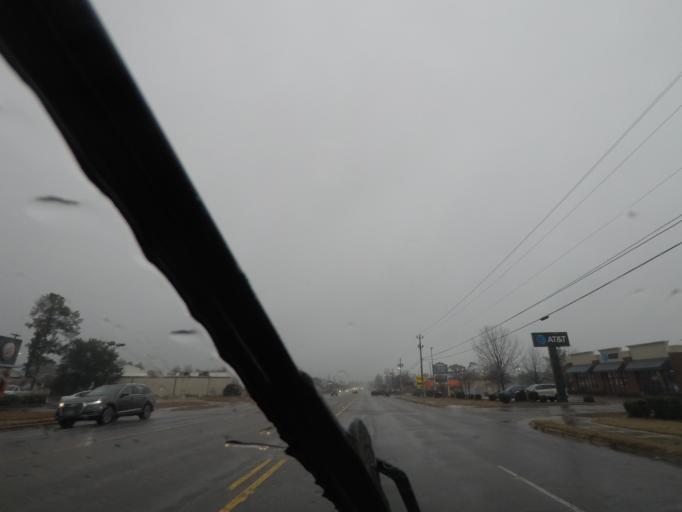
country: US
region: North Carolina
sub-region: Moore County
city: Southern Pines
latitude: 35.1565
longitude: -79.4140
